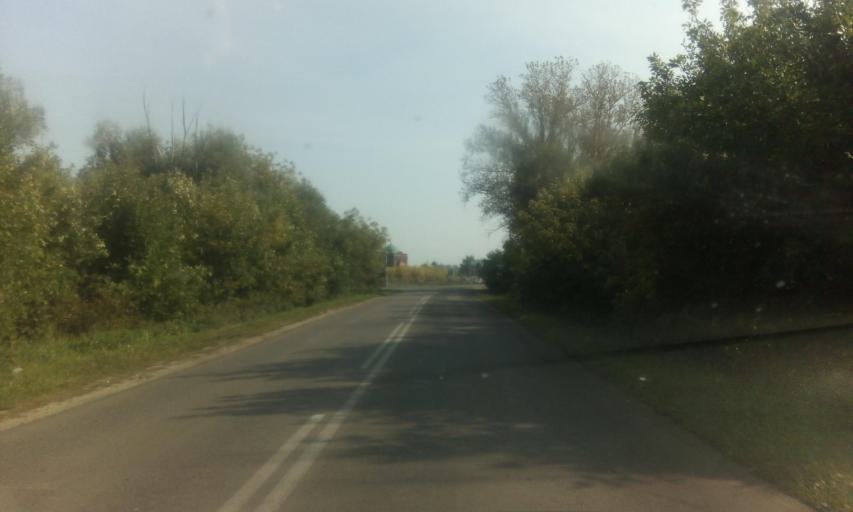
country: RU
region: Tula
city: Uzlovaya
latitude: 53.9746
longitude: 38.1310
